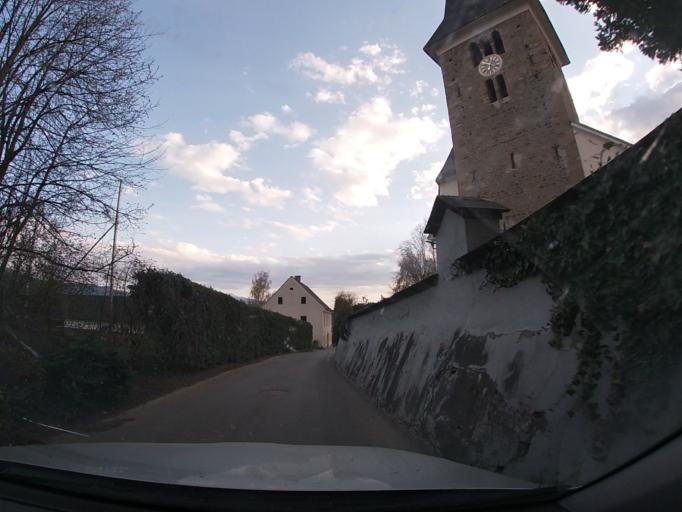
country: AT
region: Styria
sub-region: Politischer Bezirk Murtal
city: Kobenz
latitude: 47.2471
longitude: 14.8458
